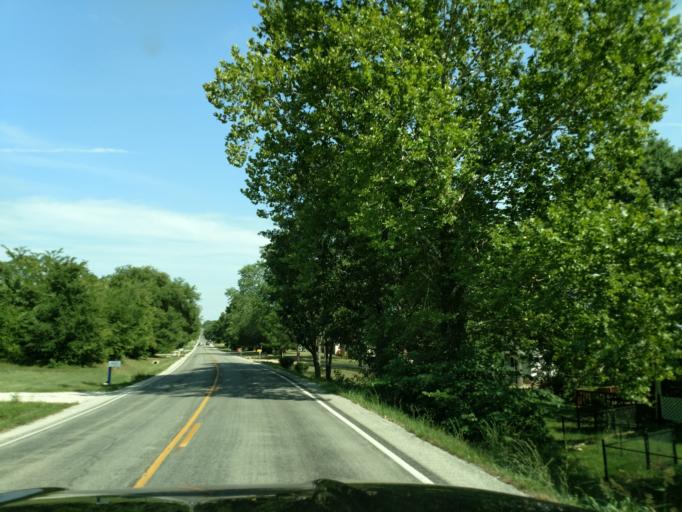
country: US
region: Missouri
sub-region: Barry County
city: Shell Knob
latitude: 36.6185
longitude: -93.6077
